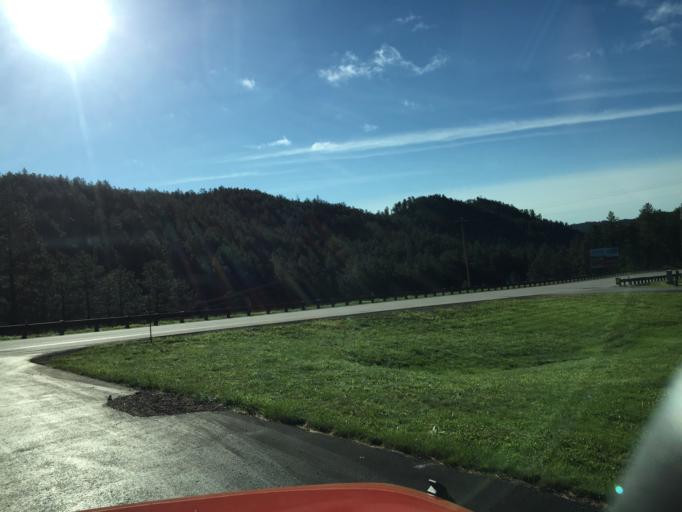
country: US
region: South Dakota
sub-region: Pennington County
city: Colonial Pine Hills
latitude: 43.9146
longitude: -103.4402
